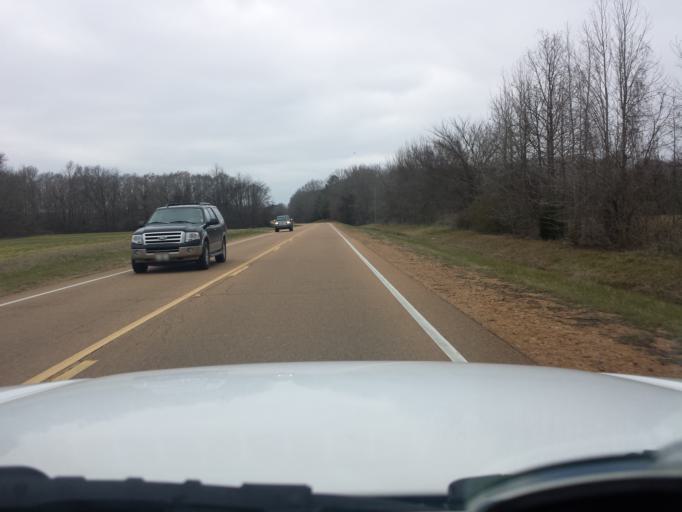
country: US
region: Mississippi
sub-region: Madison County
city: Canton
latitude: 32.7360
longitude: -90.1175
